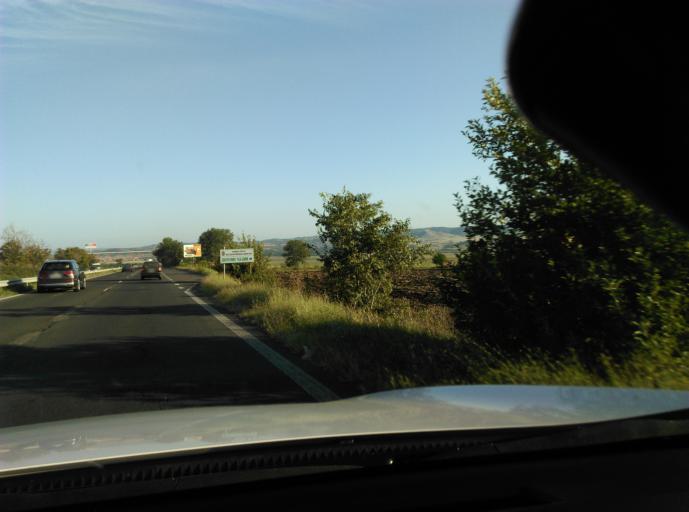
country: BG
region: Burgas
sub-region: Obshtina Burgas
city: Burgas
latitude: 42.5709
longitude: 27.4143
